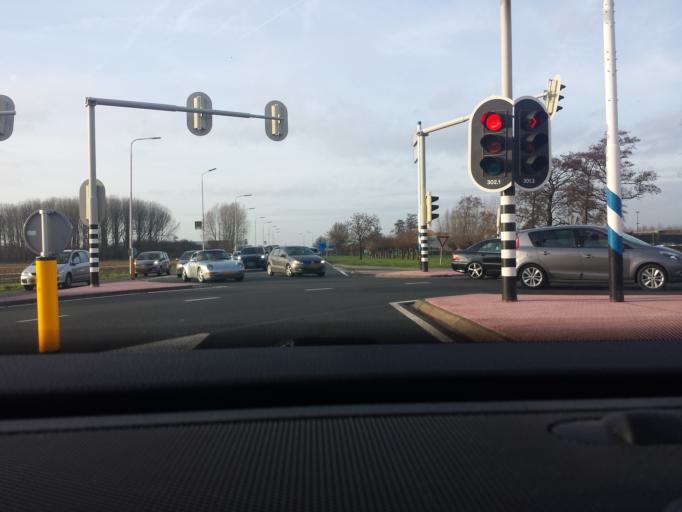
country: NL
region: Gelderland
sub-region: Gemeente Duiven
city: Duiven
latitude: 51.9578
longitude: 6.0223
